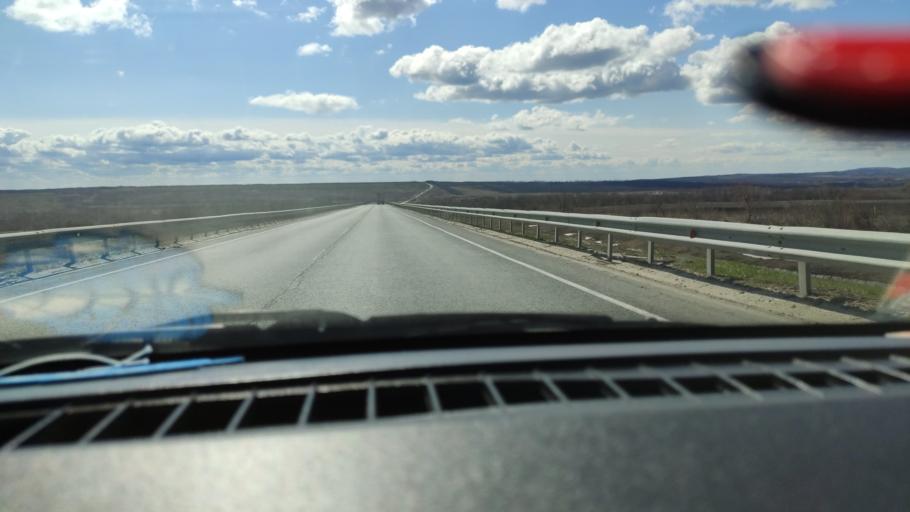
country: RU
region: Saratov
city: Dukhovnitskoye
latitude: 52.7515
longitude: 48.2478
